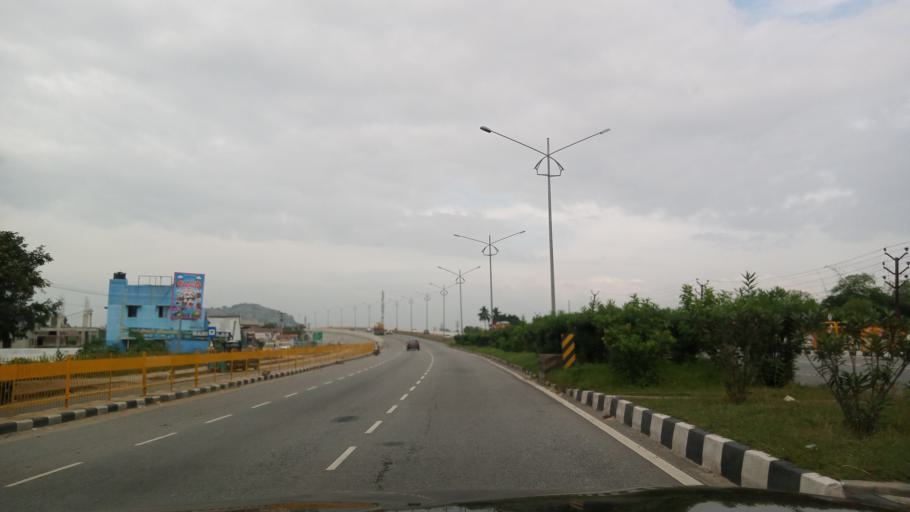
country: IN
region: Tamil Nadu
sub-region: Krishnagiri
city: Krishnagiri
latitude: 12.5129
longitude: 78.2288
